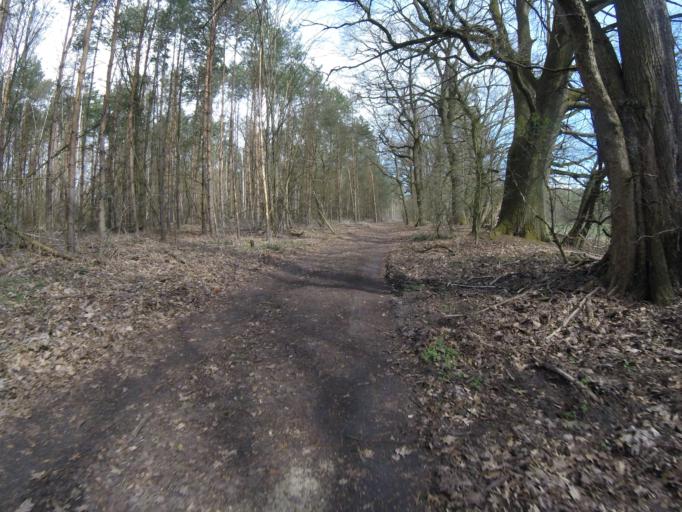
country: DE
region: Brandenburg
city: Bestensee
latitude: 52.2405
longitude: 13.6075
